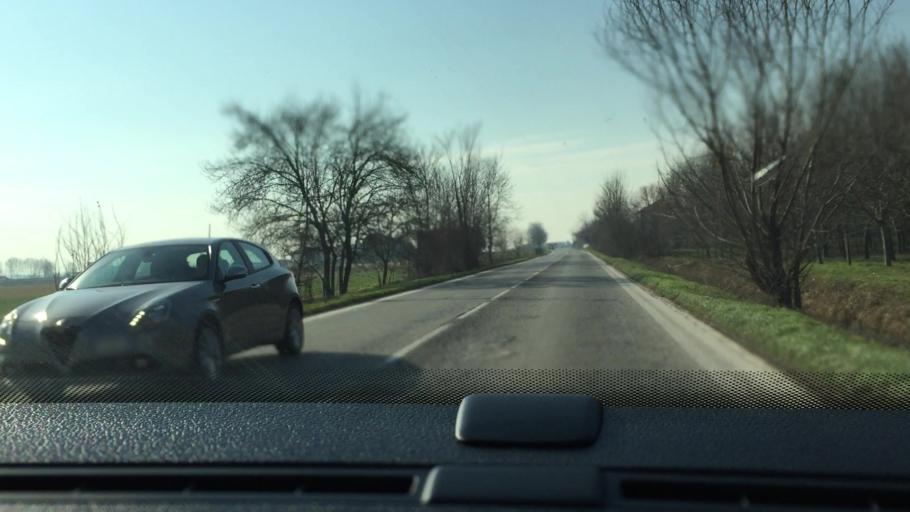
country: IT
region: Lombardy
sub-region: Provincia di Mantova
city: Goito
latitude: 45.2385
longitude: 10.6446
